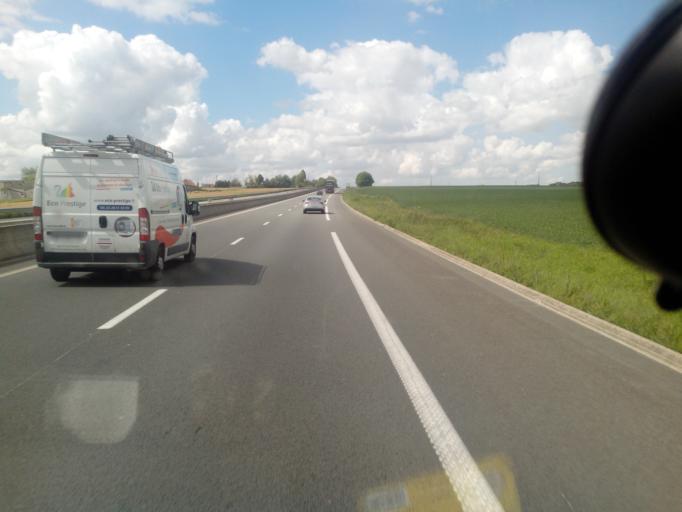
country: FR
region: Nord-Pas-de-Calais
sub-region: Departement du Nord
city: Godewaersvelde
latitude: 50.7617
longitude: 2.6421
